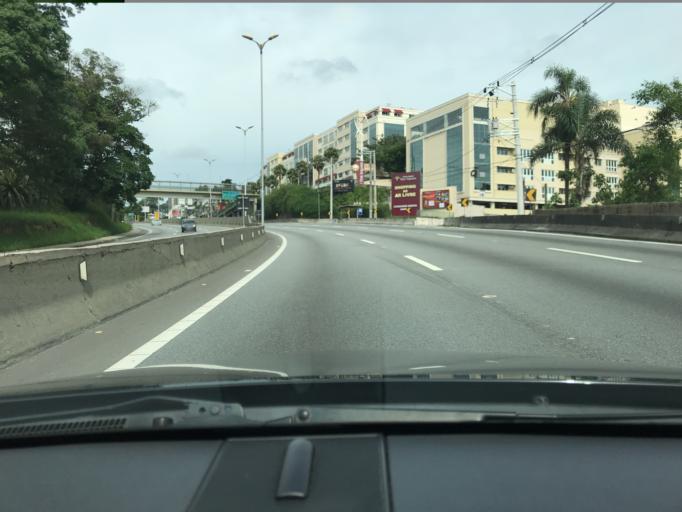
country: BR
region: Sao Paulo
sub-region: Taboao Da Serra
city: Taboao da Serra
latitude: -23.5908
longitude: -46.8225
